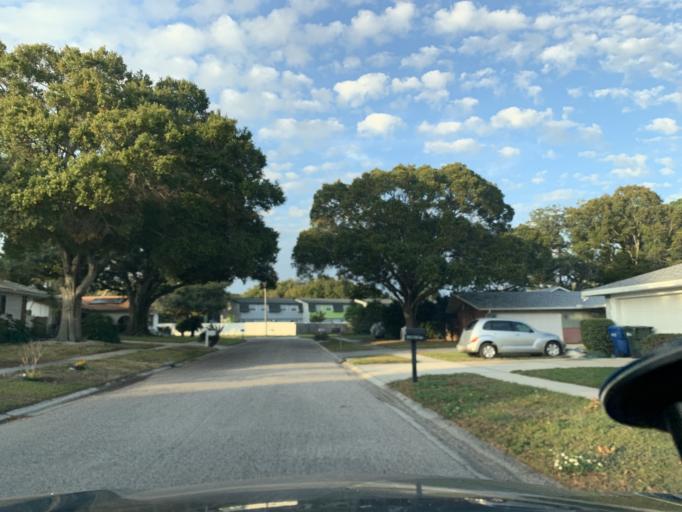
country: US
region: Florida
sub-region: Pinellas County
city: Ridgecrest
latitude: 27.8925
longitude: -82.7934
